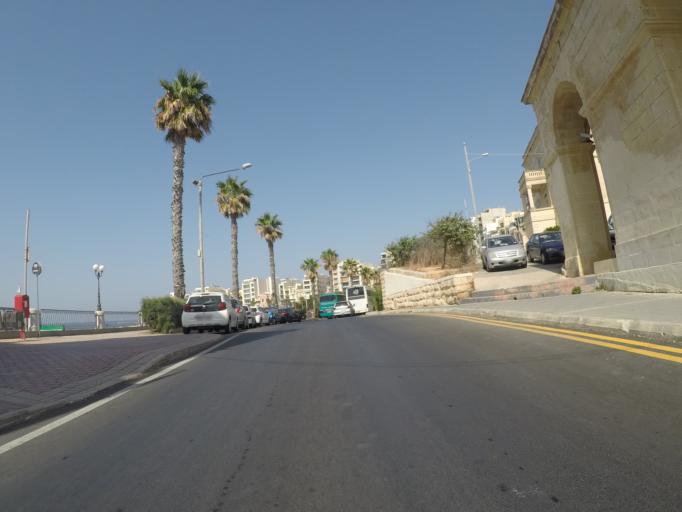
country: MT
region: Saint Paul's Bay
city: San Pawl il-Bahar
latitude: 35.9494
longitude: 14.4069
